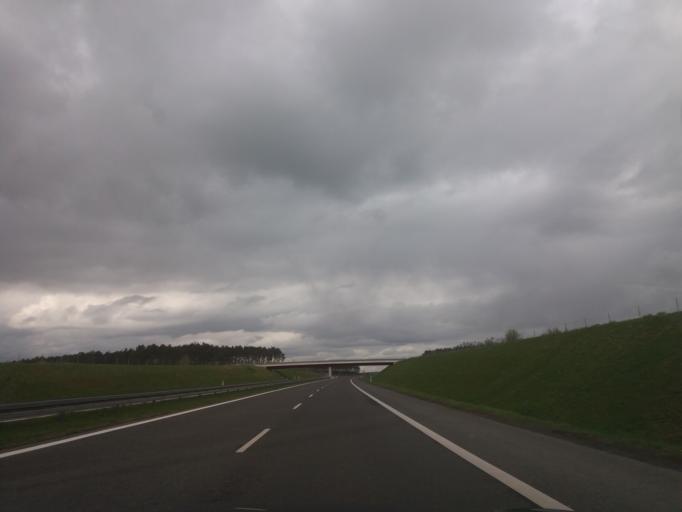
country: PL
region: Lubusz
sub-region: Powiat swiebodzinski
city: Swiebodzin
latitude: 52.3085
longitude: 15.5446
